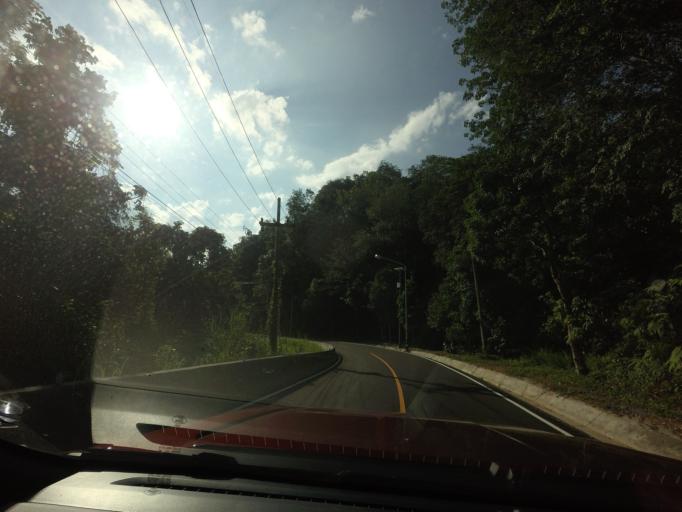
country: TH
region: Yala
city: Than To
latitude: 6.1287
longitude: 101.2977
